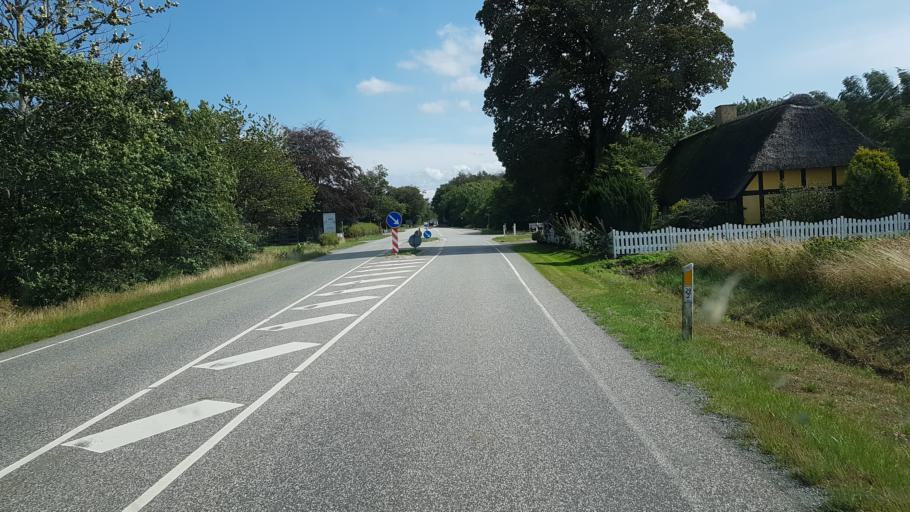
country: DK
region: South Denmark
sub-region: Billund Kommune
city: Billund
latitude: 55.6677
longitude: 9.1944
